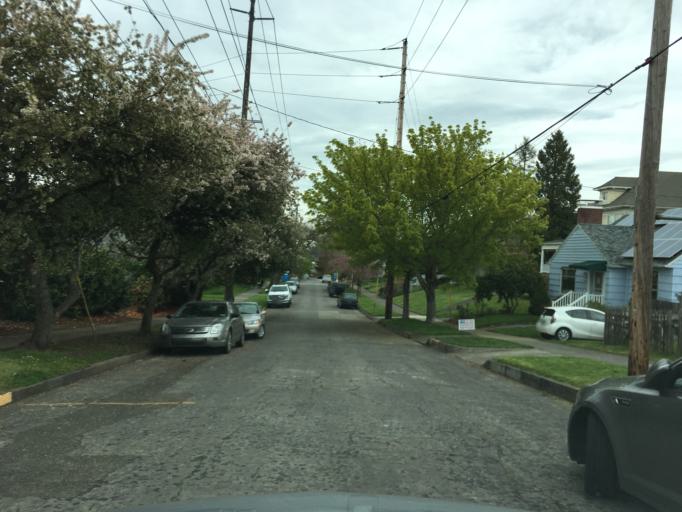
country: US
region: Oregon
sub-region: Multnomah County
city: Lents
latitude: 45.5198
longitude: -122.6011
